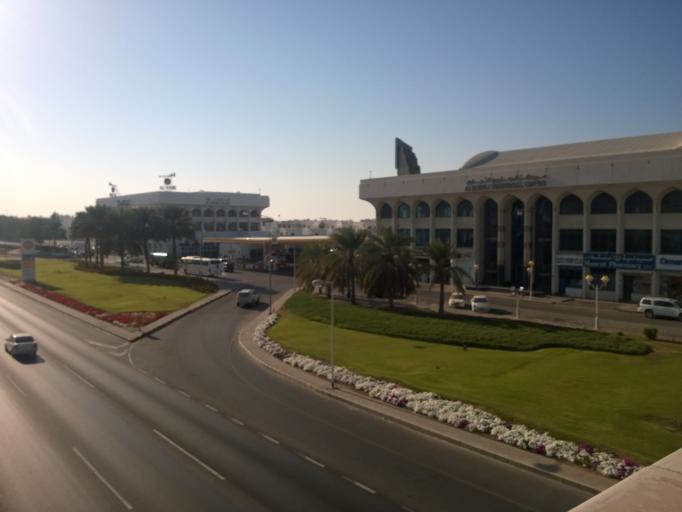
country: OM
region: Muhafazat Masqat
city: Bawshar
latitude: 23.6071
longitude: 58.4552
